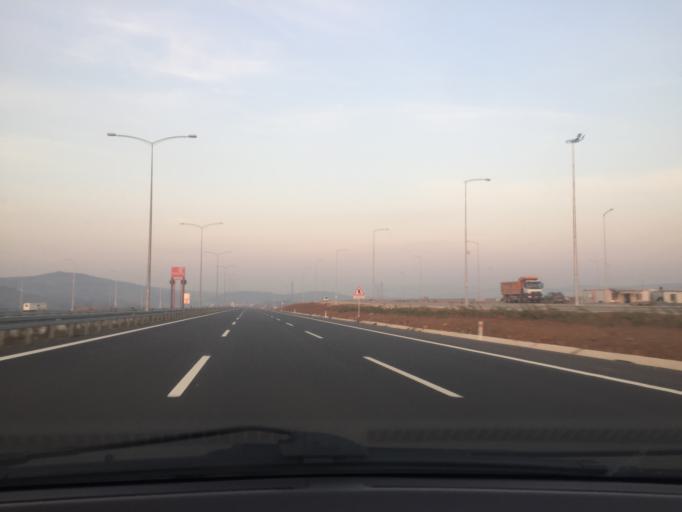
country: TR
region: Bursa
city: Mahmudiye
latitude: 40.2730
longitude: 28.6000
